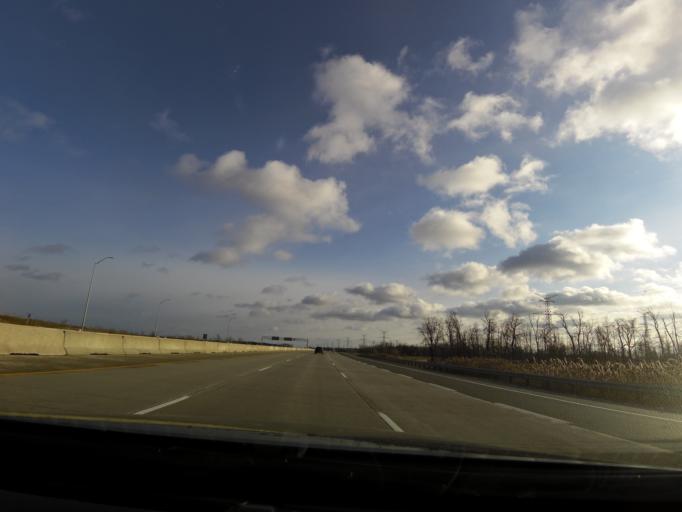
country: CA
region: Ontario
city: Mississauga
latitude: 43.5510
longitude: -79.7614
